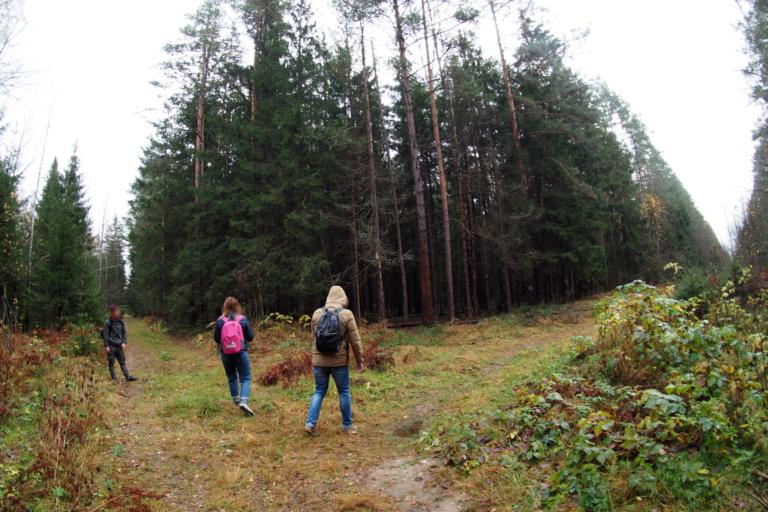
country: RU
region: Moskovskaya
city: Davydovo
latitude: 55.5605
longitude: 38.7648
